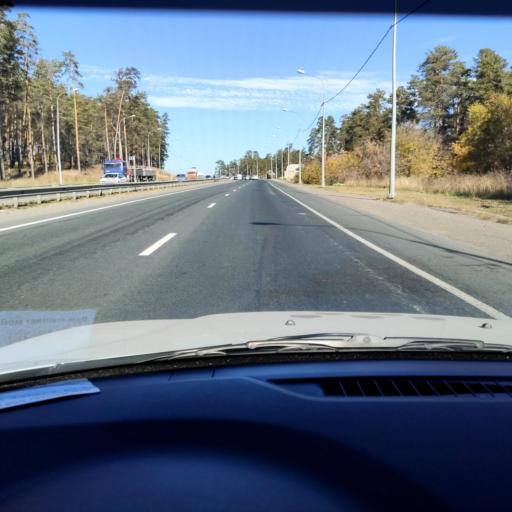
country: RU
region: Samara
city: Zhigulevsk
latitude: 53.5357
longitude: 49.5164
